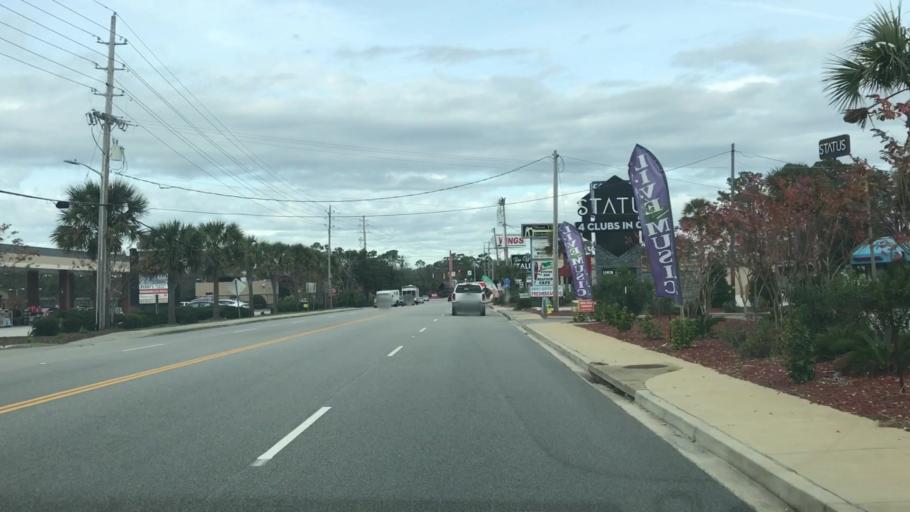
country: US
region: South Carolina
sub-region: Horry County
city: North Myrtle Beach
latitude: 33.7769
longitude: -78.7913
